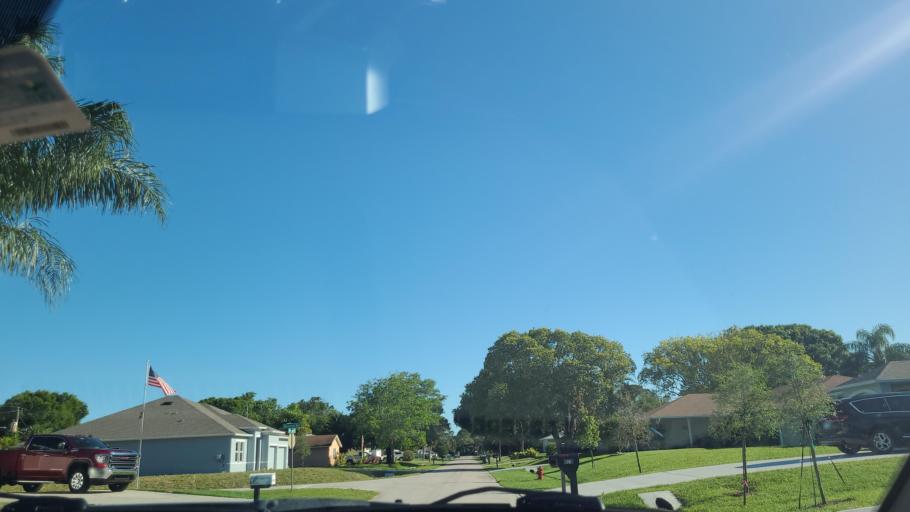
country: US
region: Florida
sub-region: Indian River County
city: Sebastian
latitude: 27.8034
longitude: -80.4912
